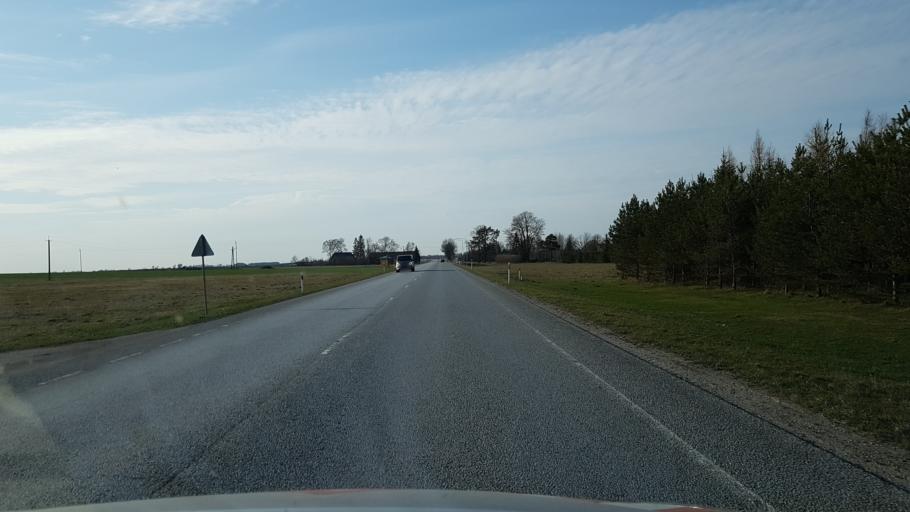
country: EE
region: Laeaene-Virumaa
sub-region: Haljala vald
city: Haljala
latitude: 59.4152
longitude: 26.2896
